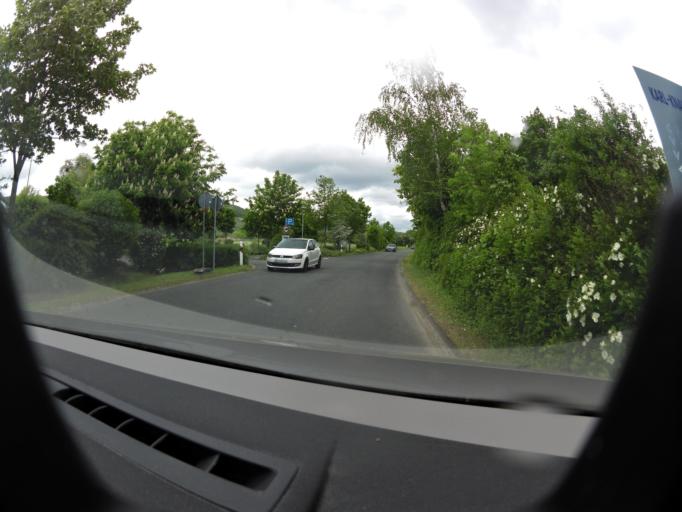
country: DE
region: Bavaria
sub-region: Regierungsbezirk Unterfranken
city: Iphofen
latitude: 49.7064
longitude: 10.2644
